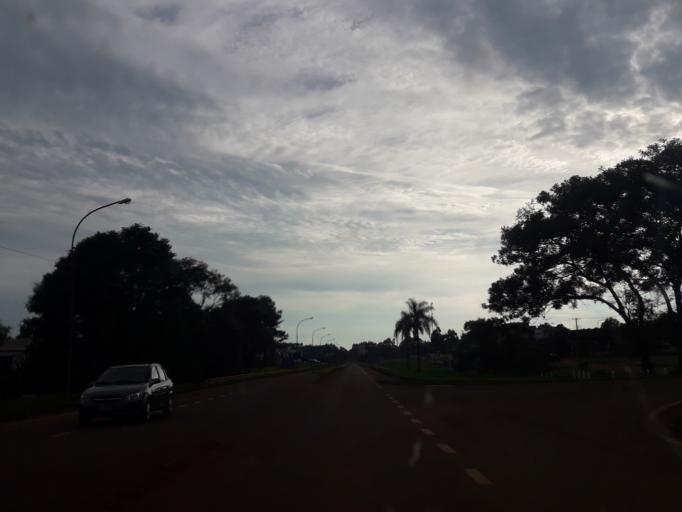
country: AR
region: Misiones
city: Dos de Mayo
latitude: -26.9913
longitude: -54.4877
